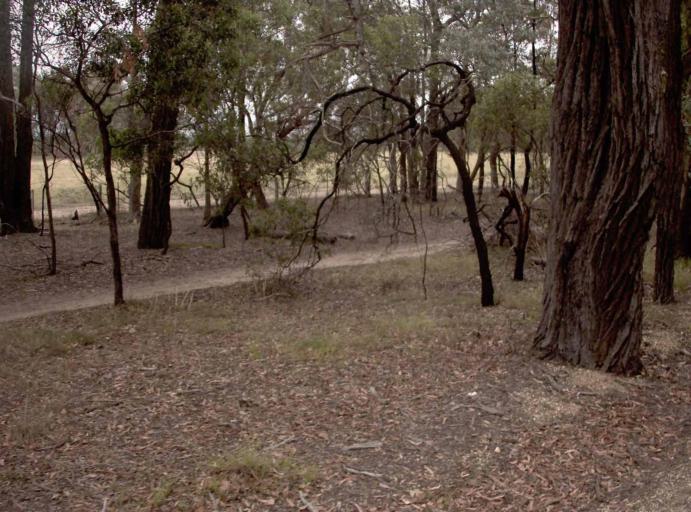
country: AU
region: Victoria
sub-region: Wellington
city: Heyfield
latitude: -37.9583
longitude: 146.7724
